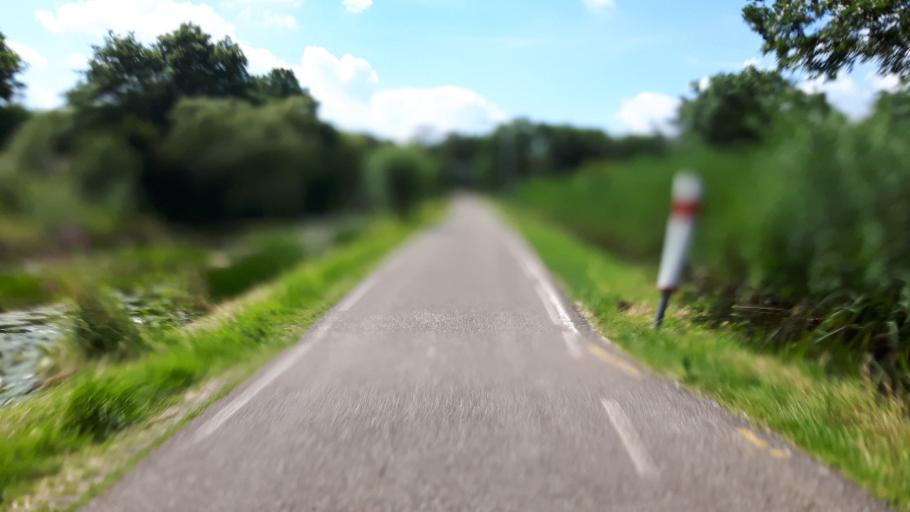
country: NL
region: South Holland
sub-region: Bodegraven-Reeuwijk
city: Reeuwijk
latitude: 52.0337
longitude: 4.7474
